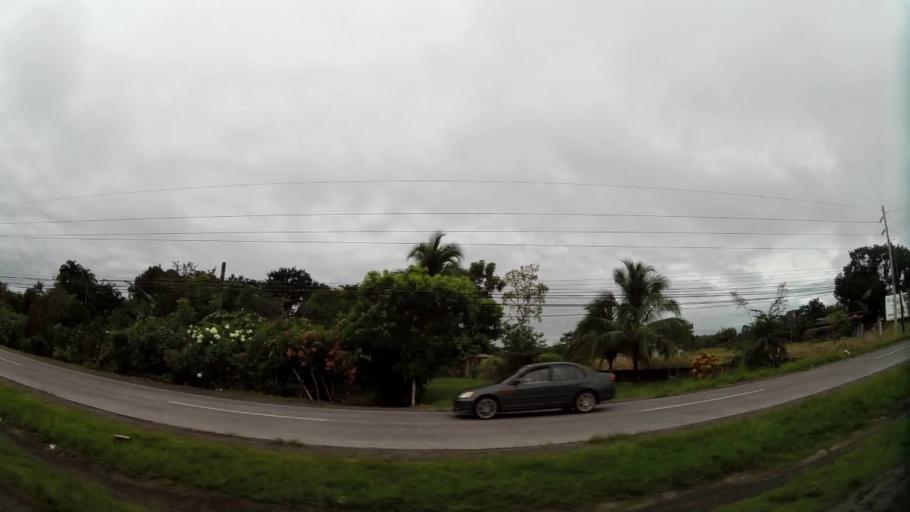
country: PA
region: Chiriqui
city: Boqueron
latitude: 8.4982
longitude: -82.5926
